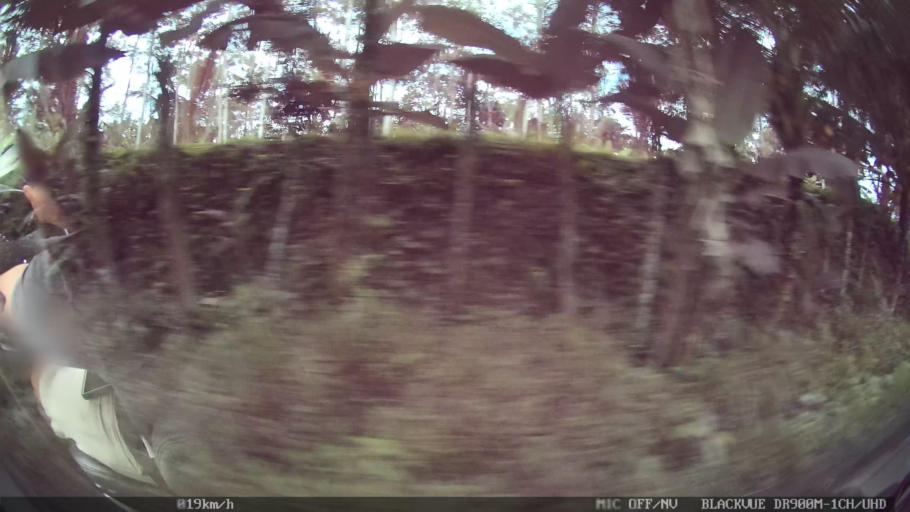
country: ID
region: Bali
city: Banjar Petak
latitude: -8.4466
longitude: 115.3229
